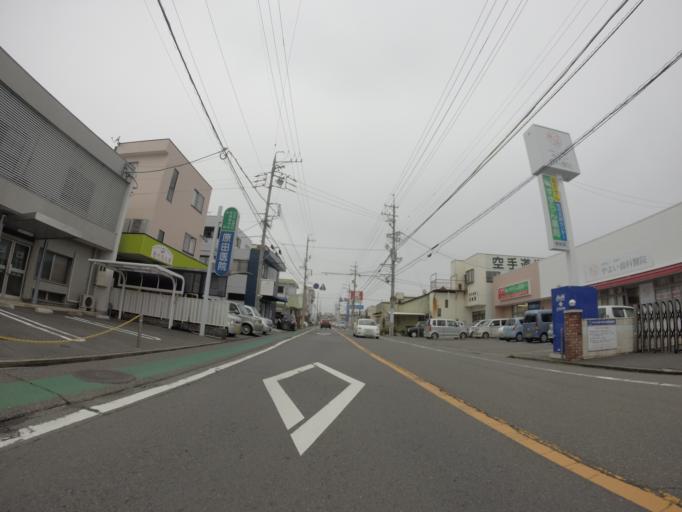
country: JP
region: Shizuoka
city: Shizuoka-shi
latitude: 34.9547
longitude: 138.3929
